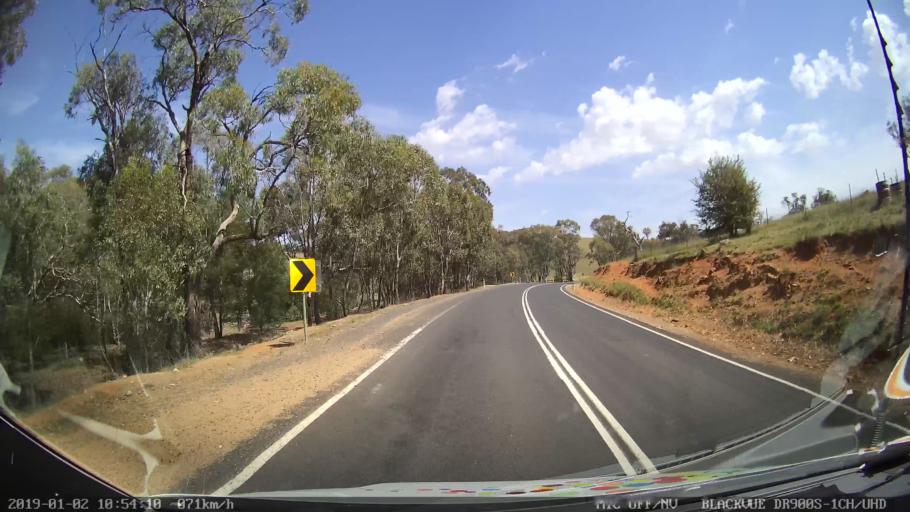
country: AU
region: New South Wales
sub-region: Cootamundra
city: Cootamundra
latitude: -34.6726
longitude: 148.2738
